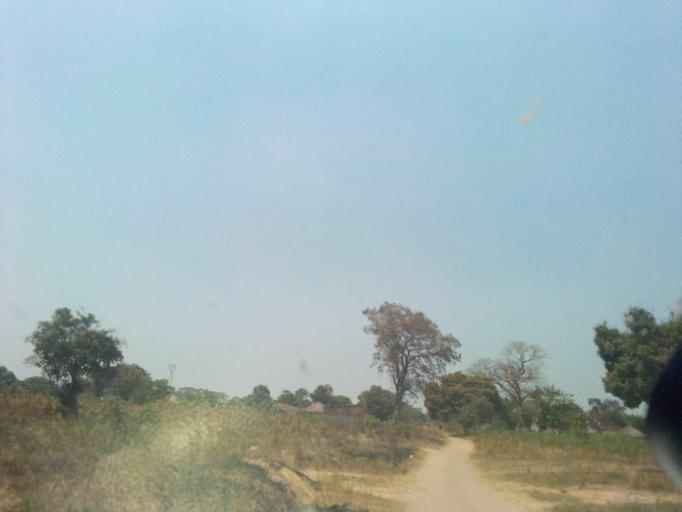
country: ZM
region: Copperbelt
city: Kataba
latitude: -12.2422
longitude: 30.3204
